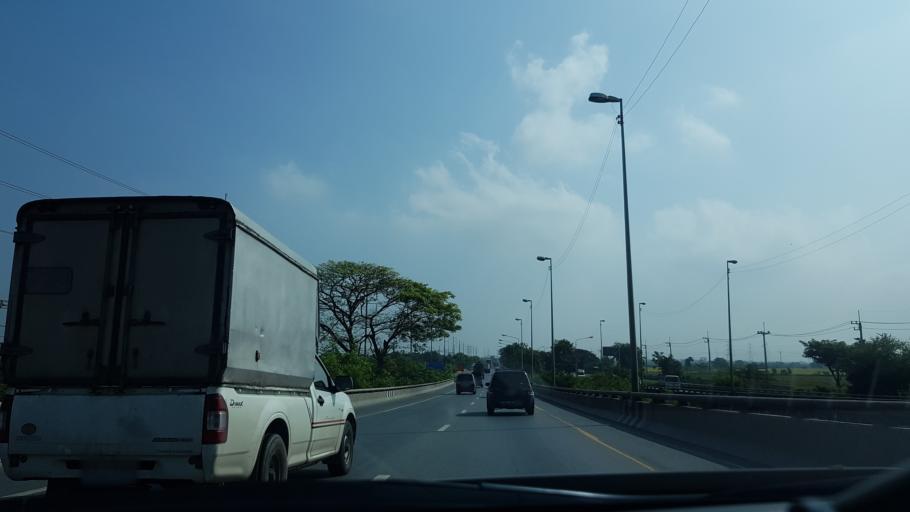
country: TH
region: Phra Nakhon Si Ayutthaya
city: Bang Pa-in
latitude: 14.1635
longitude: 100.5796
